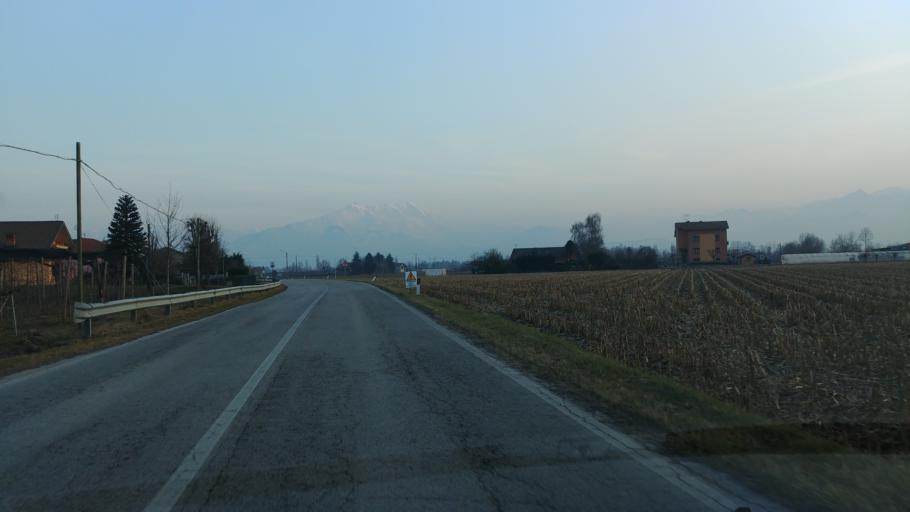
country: IT
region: Piedmont
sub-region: Provincia di Cuneo
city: Roata Rossi
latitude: 44.4169
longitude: 7.5103
